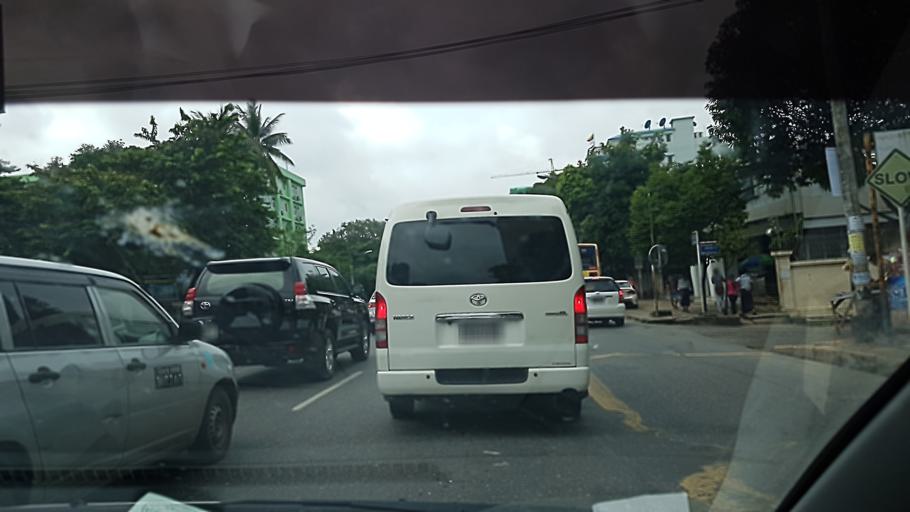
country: MM
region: Yangon
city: Yangon
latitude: 16.8089
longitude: 96.1358
